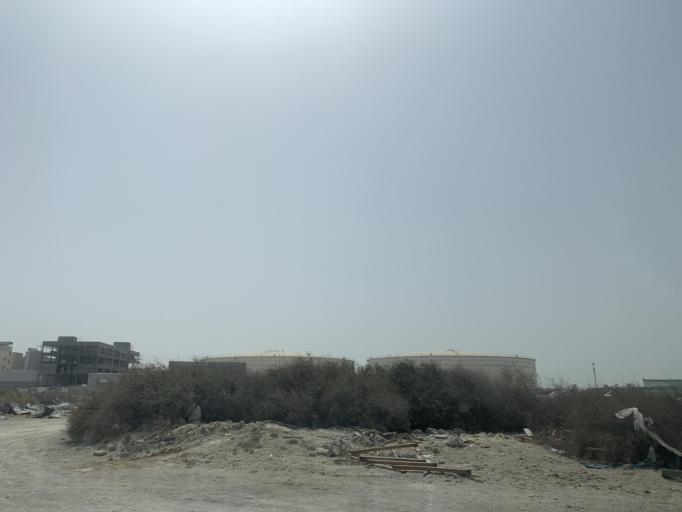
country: BH
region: Northern
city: Madinat `Isa
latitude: 26.1863
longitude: 50.5233
